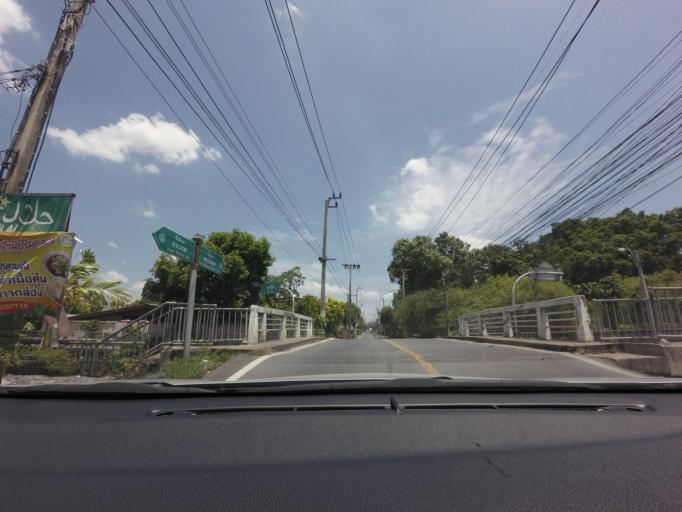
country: TH
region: Bangkok
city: Bang Na
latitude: 13.6891
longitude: 100.6382
